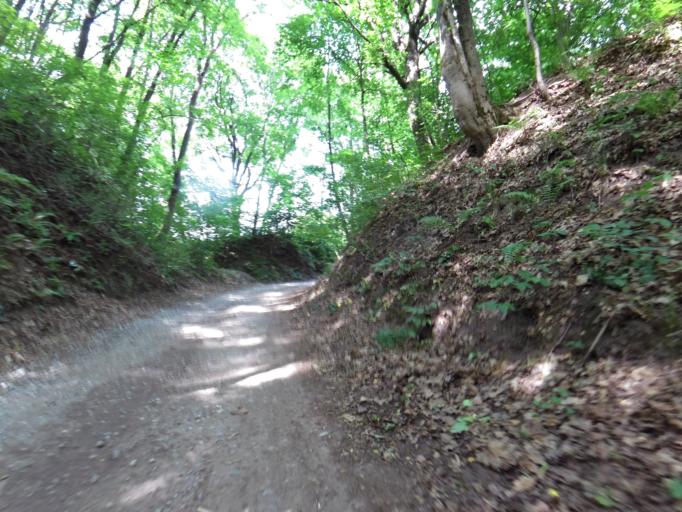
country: LT
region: Vilnius County
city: Rasos
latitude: 54.6906
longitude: 25.3592
